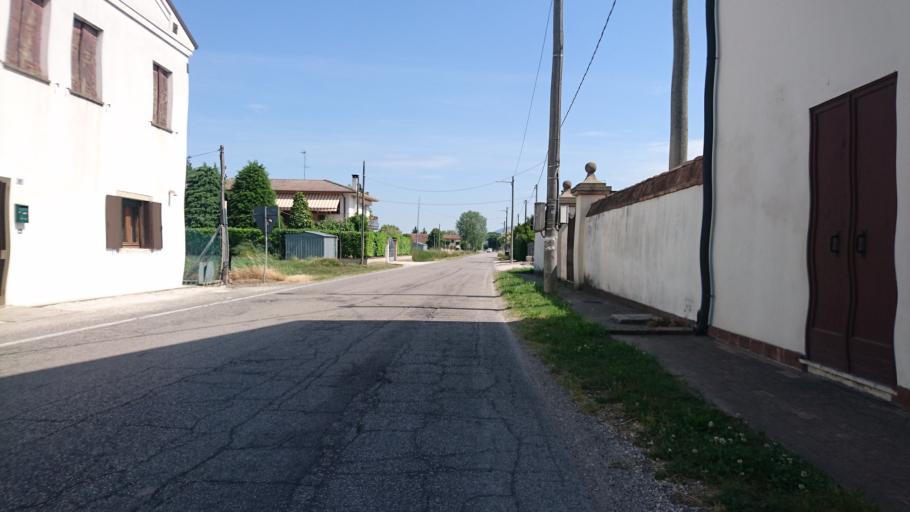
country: IT
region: Veneto
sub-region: Provincia di Padova
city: Ospedaletto Euganeo
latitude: 45.2136
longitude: 11.5980
